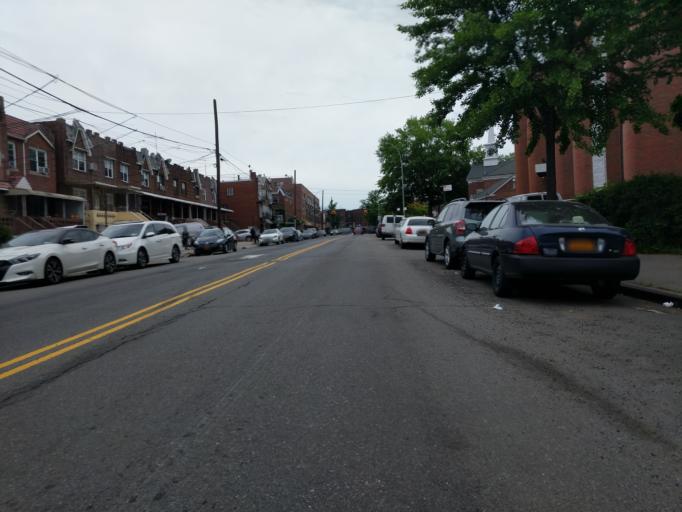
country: US
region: New York
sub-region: Queens County
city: Borough of Queens
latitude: 40.7407
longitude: -73.8761
